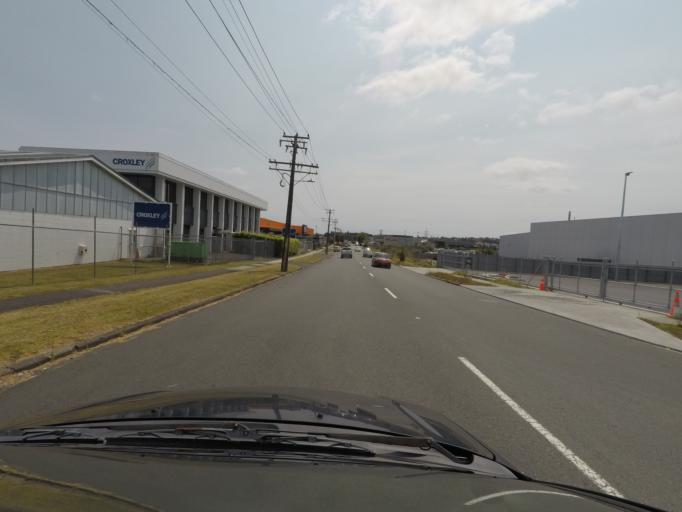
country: NZ
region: Auckland
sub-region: Auckland
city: Waitakere
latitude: -36.9138
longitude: 174.6876
